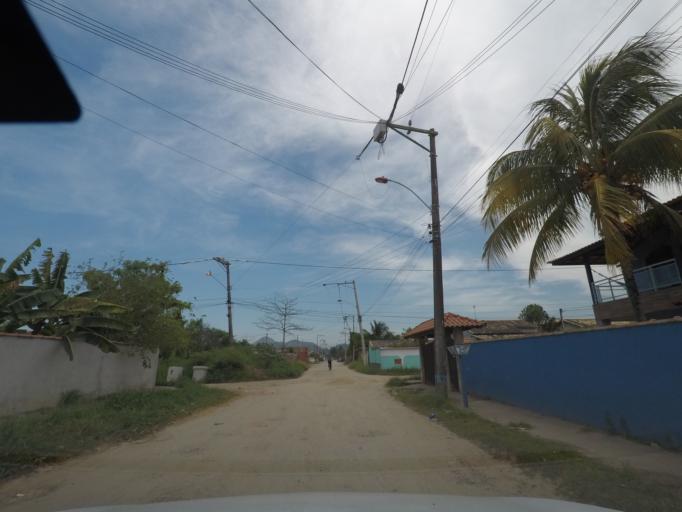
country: BR
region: Rio de Janeiro
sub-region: Marica
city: Marica
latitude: -22.9620
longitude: -42.9557
